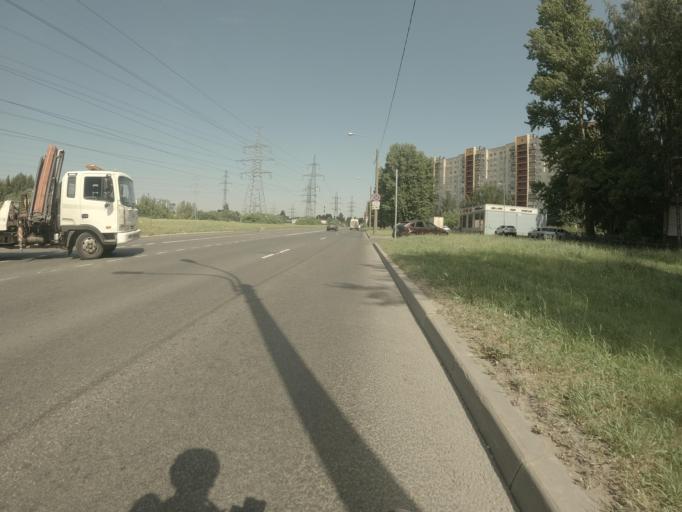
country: RU
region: St.-Petersburg
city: Krasnogvargeisky
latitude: 59.9503
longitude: 30.4609
